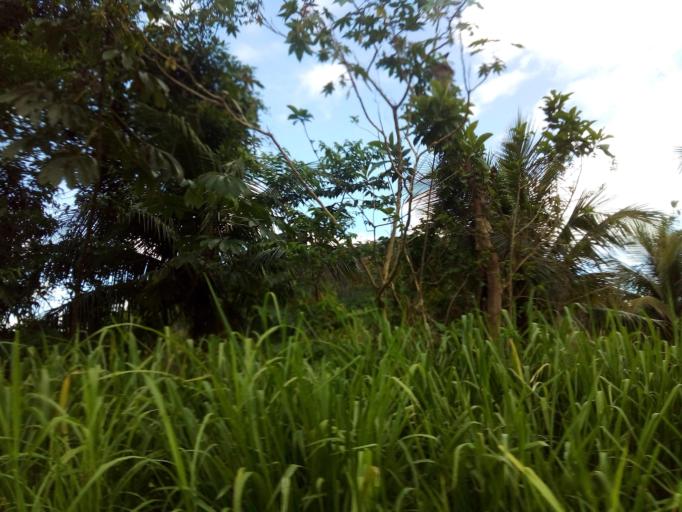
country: BR
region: Espirito Santo
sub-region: Ibiracu
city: Ibiracu
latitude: -19.8676
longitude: -40.3614
